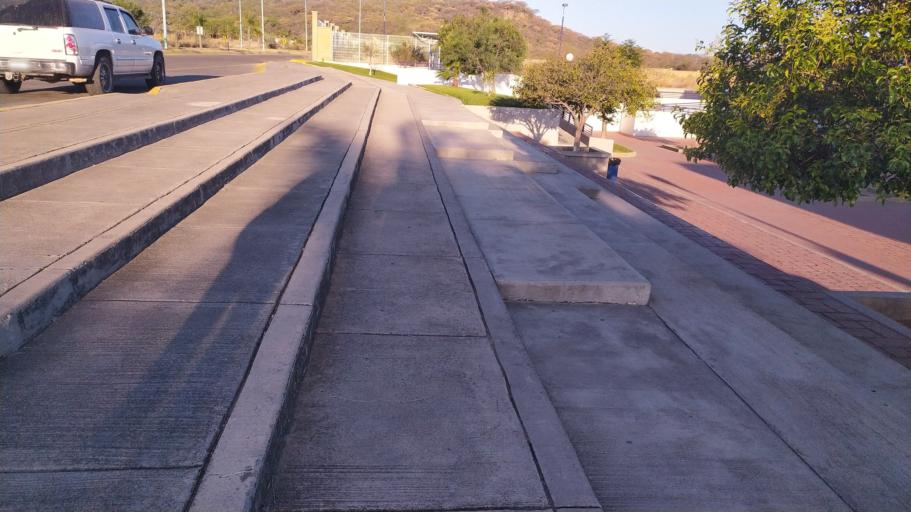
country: MX
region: Guanajuato
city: Ciudad Manuel Doblado
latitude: 20.7560
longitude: -101.9671
